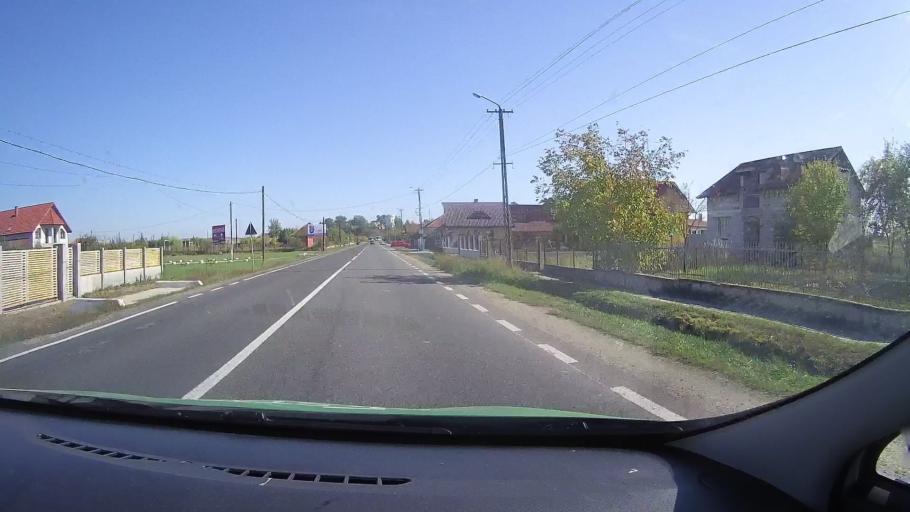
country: RO
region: Satu Mare
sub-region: Oras Ardud
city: Ardud
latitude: 47.6521
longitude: 22.8889
